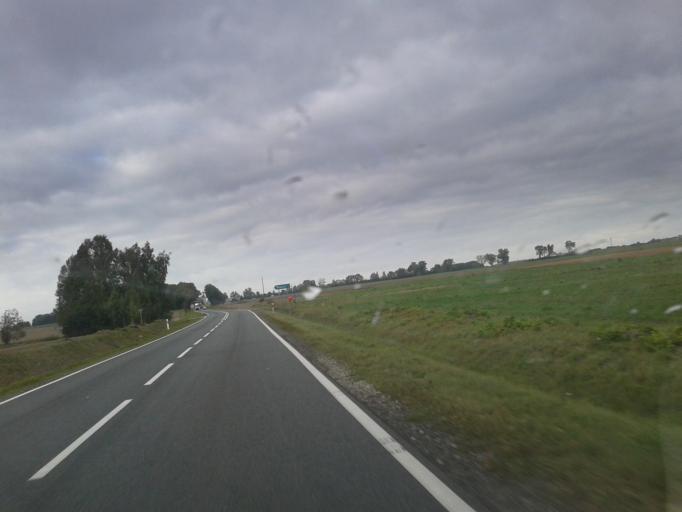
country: PL
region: Kujawsko-Pomorskie
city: Kamien Krajenski
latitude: 53.4932
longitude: 17.5116
